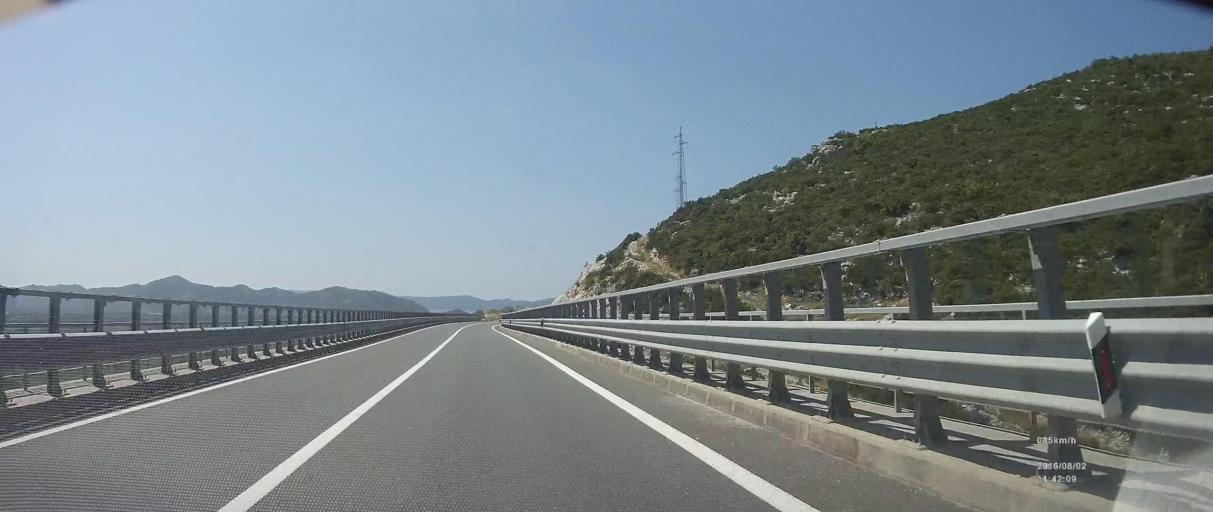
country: HR
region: Dubrovacko-Neretvanska
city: Komin
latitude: 43.0562
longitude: 17.4897
